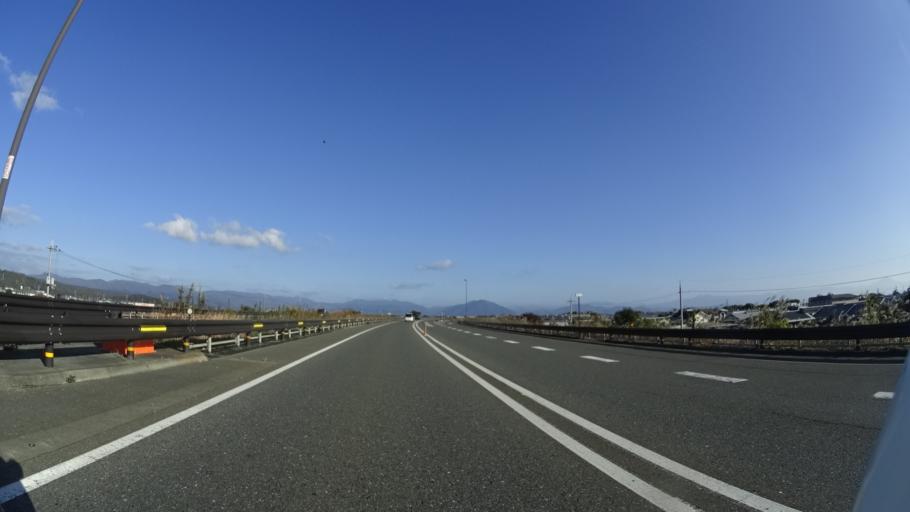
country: JP
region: Shiga Prefecture
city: Kitahama
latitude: 35.3486
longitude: 136.0433
